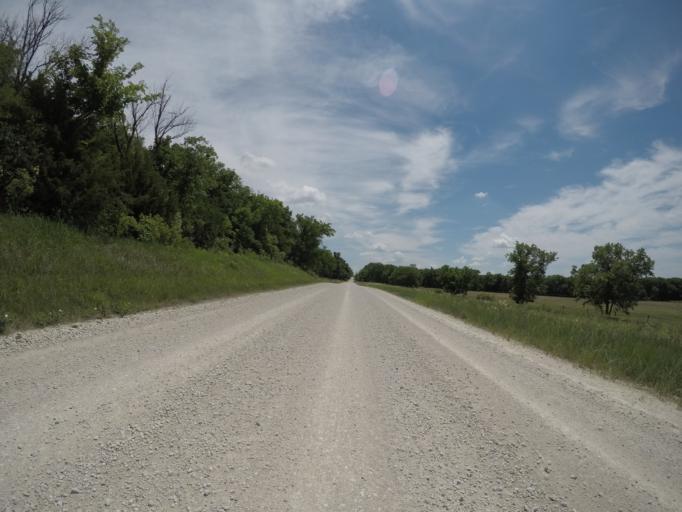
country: US
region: Kansas
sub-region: Wabaunsee County
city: Alma
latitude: 38.9362
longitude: -96.2345
